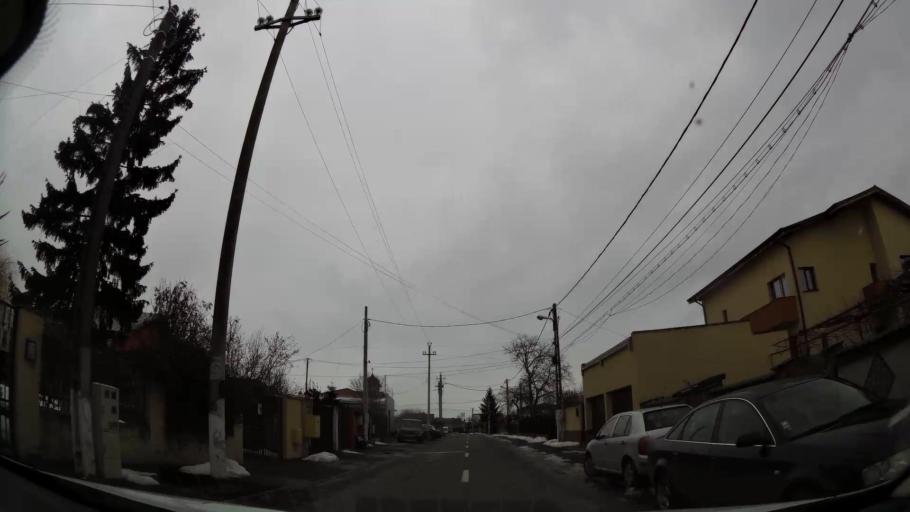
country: RO
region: Ilfov
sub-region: Comuna Otopeni
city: Otopeni
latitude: 44.5518
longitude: 26.0879
